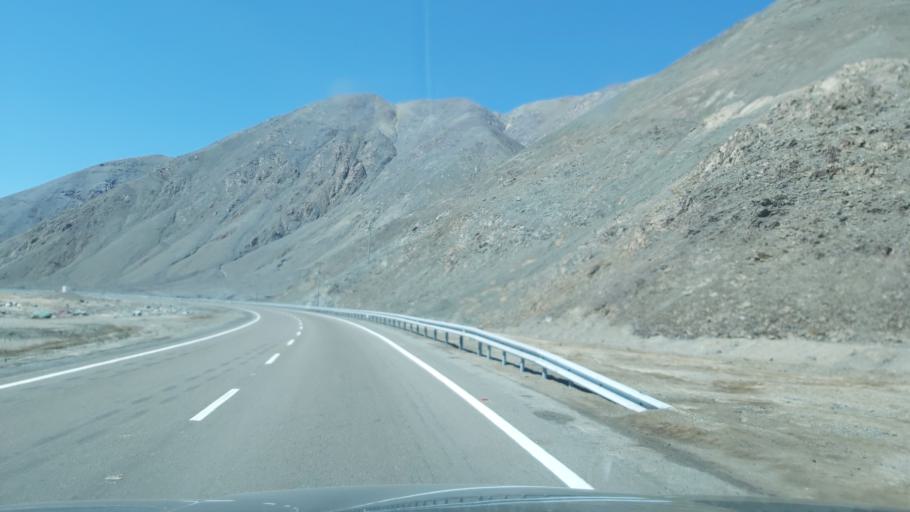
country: CL
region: Atacama
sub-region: Provincia de Chanaral
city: Diego de Almagro
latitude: -26.3473
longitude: -69.7423
